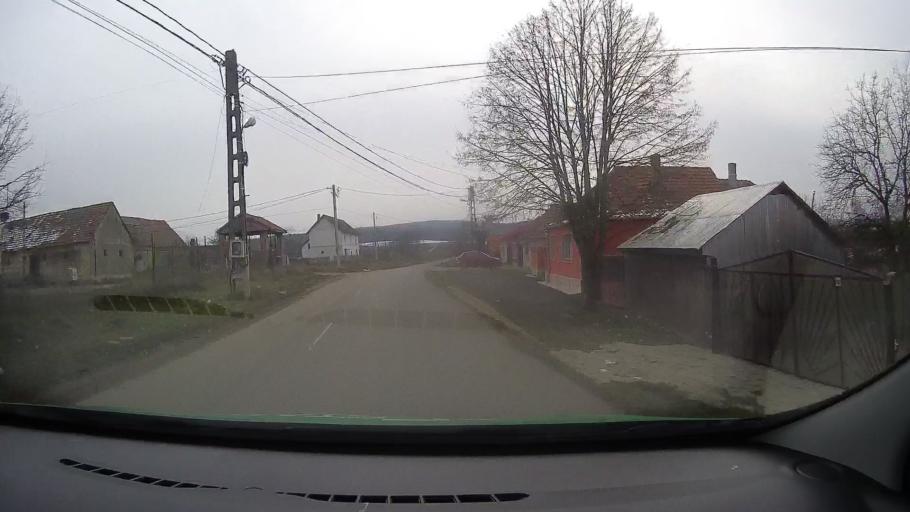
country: RO
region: Hunedoara
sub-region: Comuna Turdas
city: Turdas
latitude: 45.8470
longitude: 23.1221
